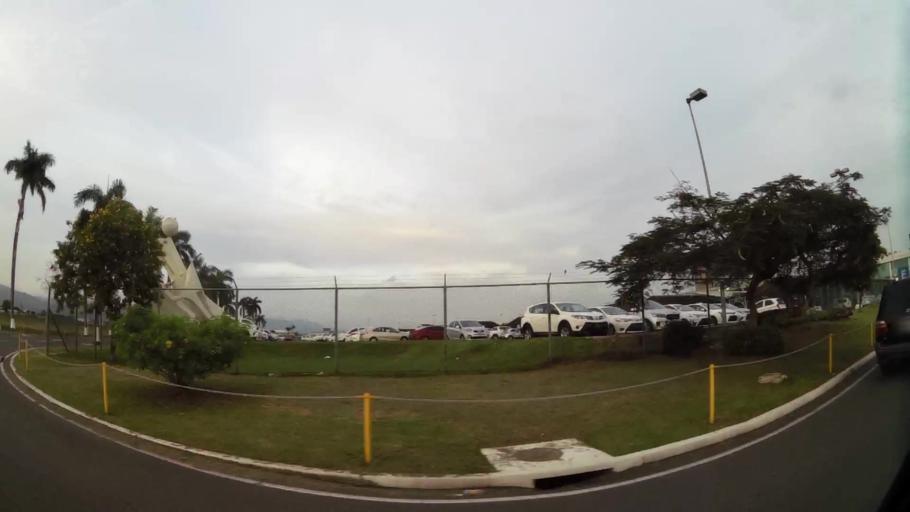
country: PA
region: Panama
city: Tocumen
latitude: 9.0670
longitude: -79.3893
